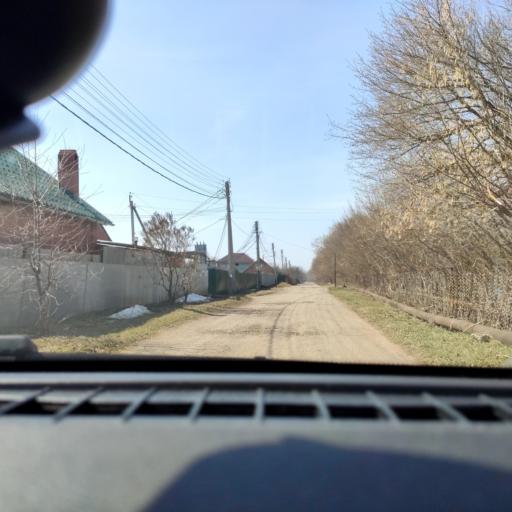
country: RU
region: Samara
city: Podstepki
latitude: 53.5203
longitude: 49.1061
